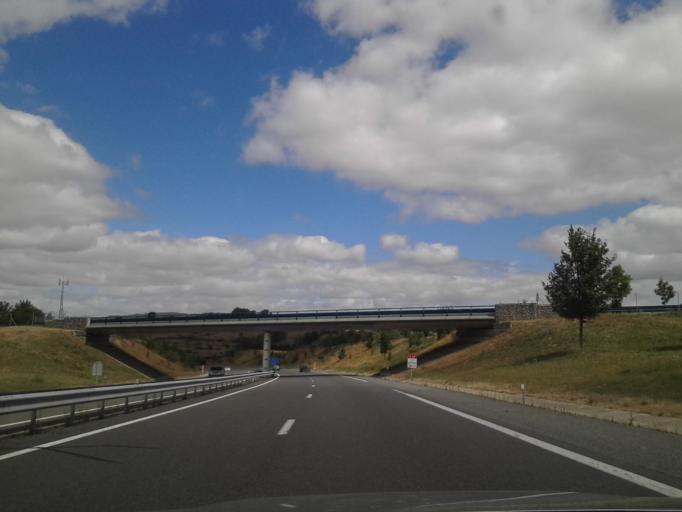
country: FR
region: Midi-Pyrenees
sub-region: Departement de l'Aveyron
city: Severac-le-Chateau
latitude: 44.3071
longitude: 3.1040
